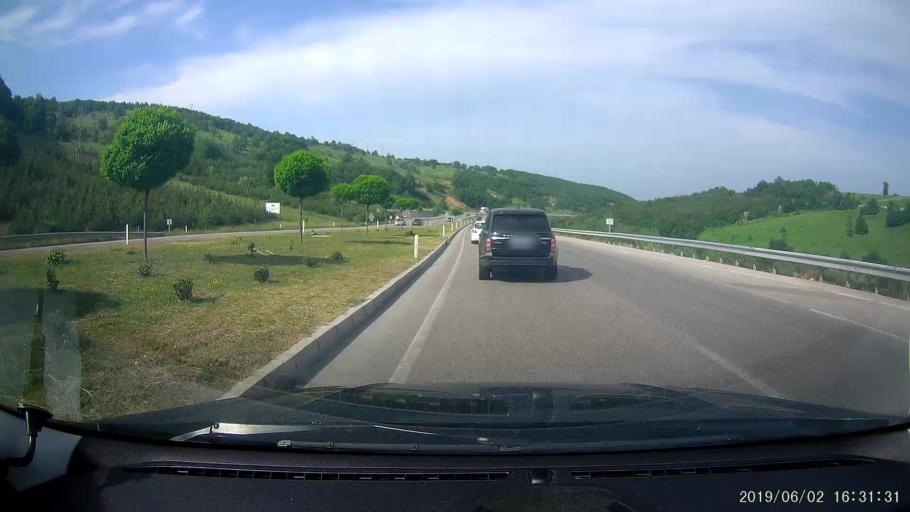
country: TR
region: Samsun
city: Ladik
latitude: 41.0328
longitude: 35.9022
